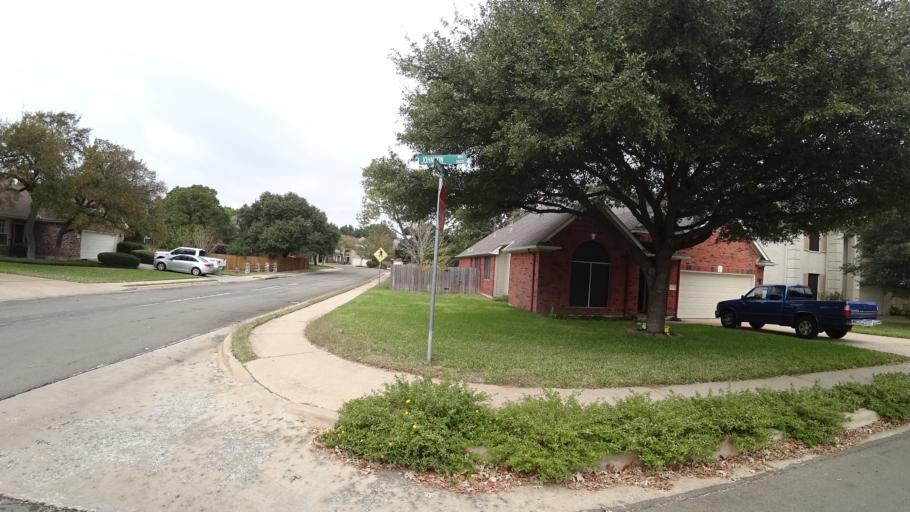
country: US
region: Texas
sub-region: Williamson County
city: Round Rock
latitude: 30.5142
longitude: -97.7039
